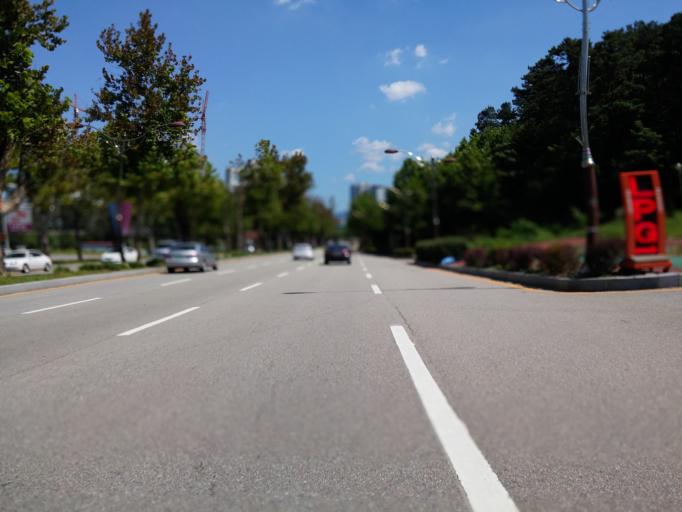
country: KR
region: Chungcheongbuk-do
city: Cheongju-si
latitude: 36.6260
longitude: 127.4173
